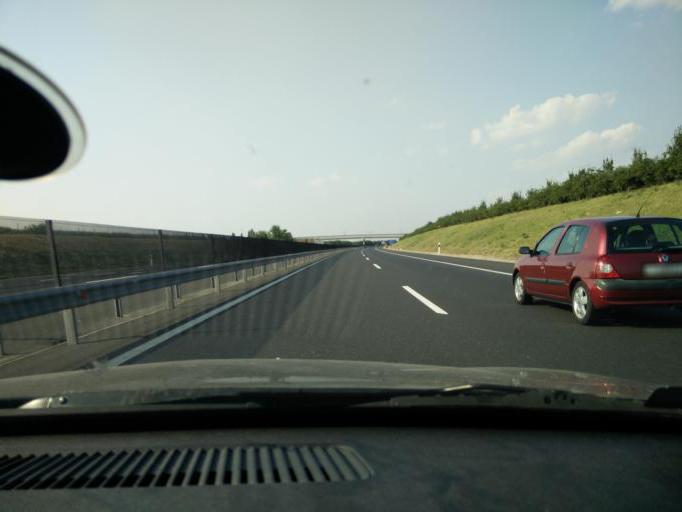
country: HU
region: Fejer
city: Rackeresztur
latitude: 47.3107
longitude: 18.8685
